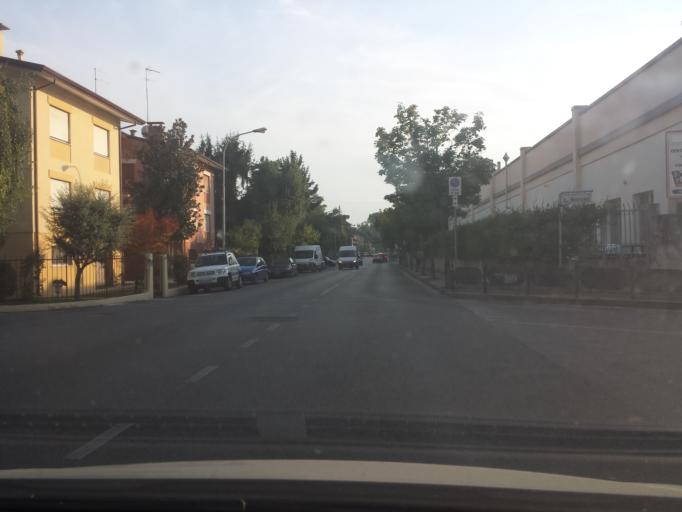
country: IT
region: Veneto
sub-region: Provincia di Venezia
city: San Dona di Piave
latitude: 45.6292
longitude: 12.5727
